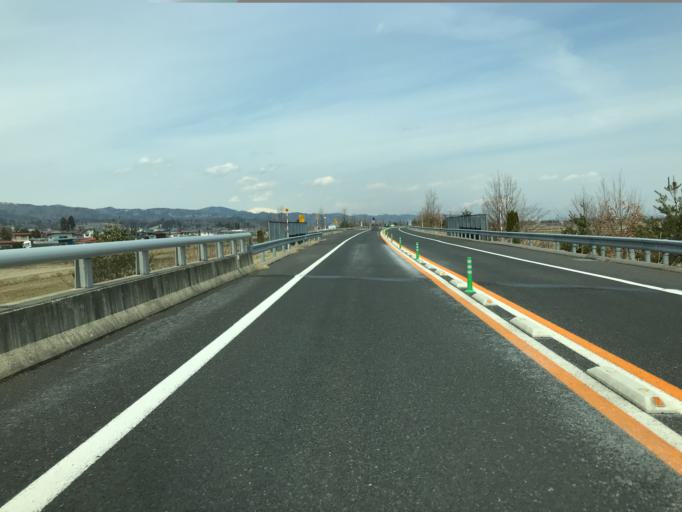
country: JP
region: Yamagata
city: Kaminoyama
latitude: 38.2290
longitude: 140.2766
